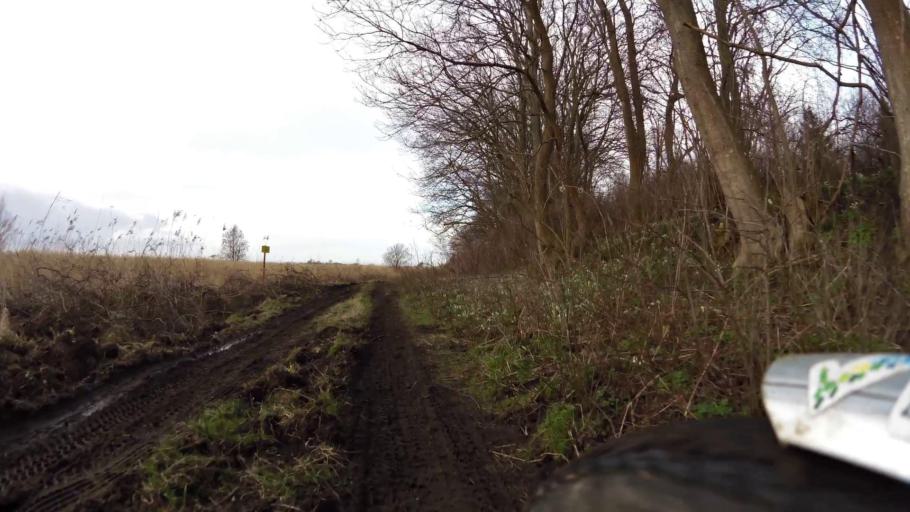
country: PL
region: West Pomeranian Voivodeship
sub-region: Powiat kamienski
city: Kamien Pomorski
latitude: 53.9245
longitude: 14.7600
